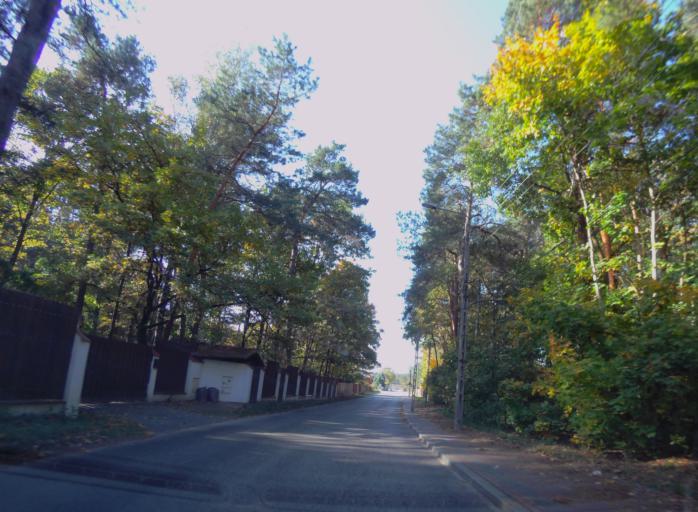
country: PL
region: Masovian Voivodeship
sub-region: Powiat otwocki
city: Jozefow
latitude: 52.1679
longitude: 21.2999
